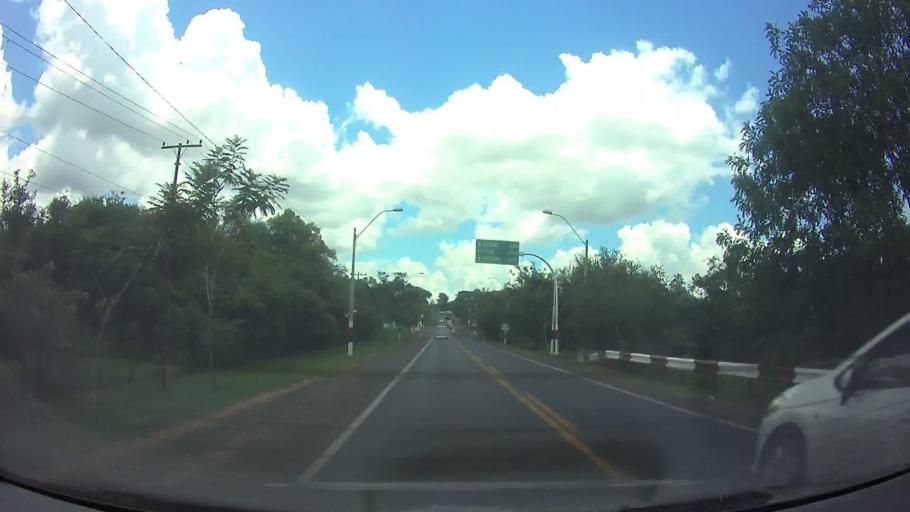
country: PY
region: Central
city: Capiata
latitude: -25.3470
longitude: -57.4159
